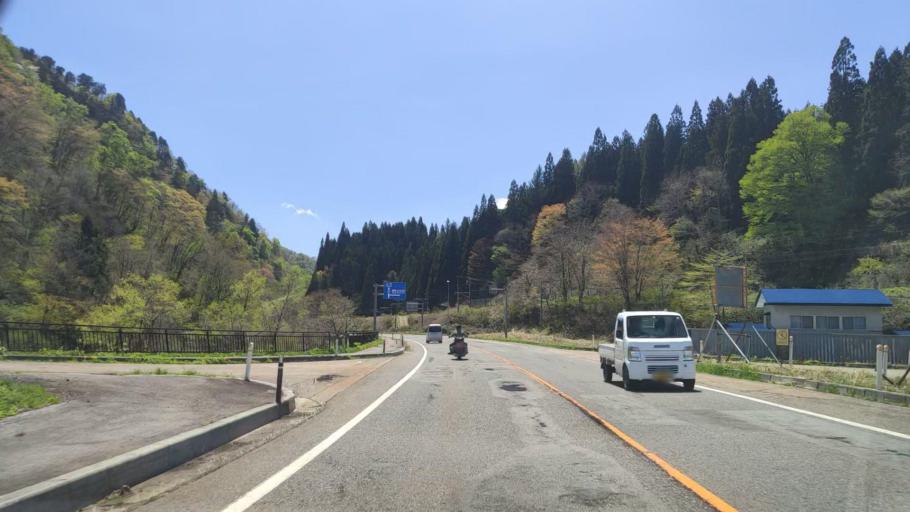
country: JP
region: Akita
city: Yuzawa
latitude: 38.9892
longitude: 140.3626
